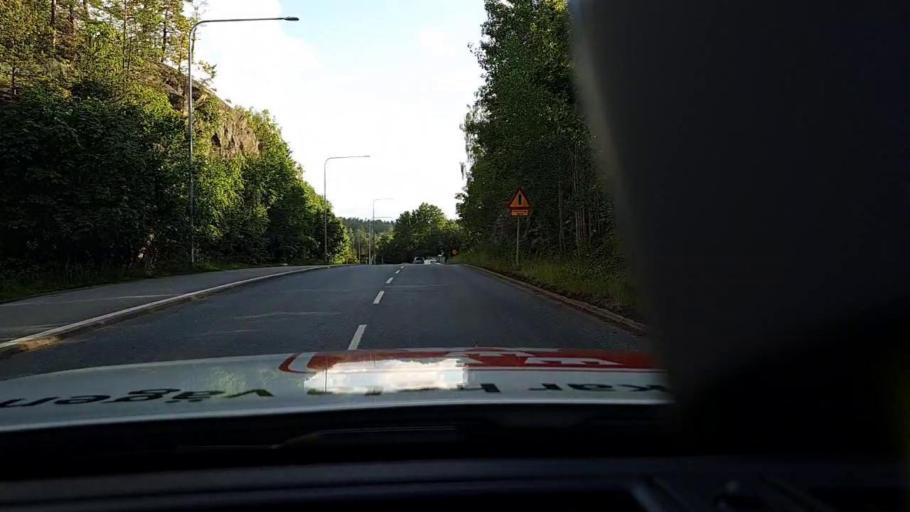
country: SE
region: Stockholm
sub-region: Huddinge Kommun
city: Huddinge
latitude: 59.2523
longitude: 17.9683
